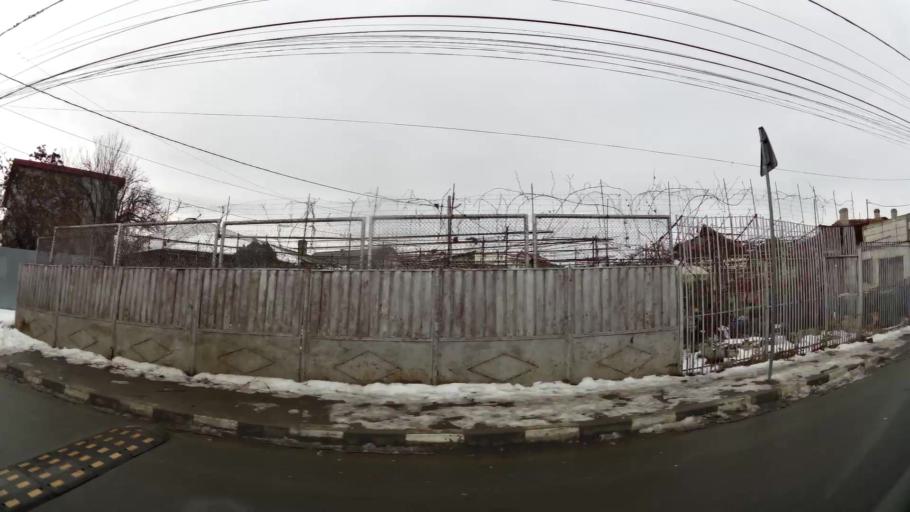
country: RO
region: Ilfov
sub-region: Comuna Pantelimon
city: Pantelimon
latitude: 44.4558
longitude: 26.2002
